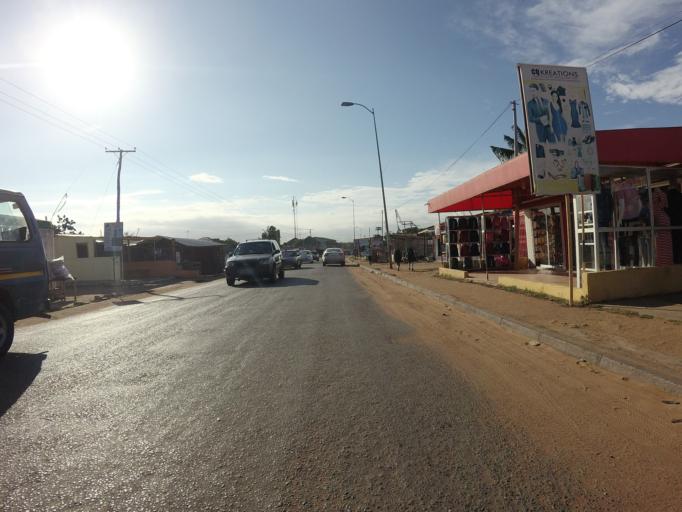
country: GH
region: Greater Accra
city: Nungua
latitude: 5.6477
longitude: -0.0616
